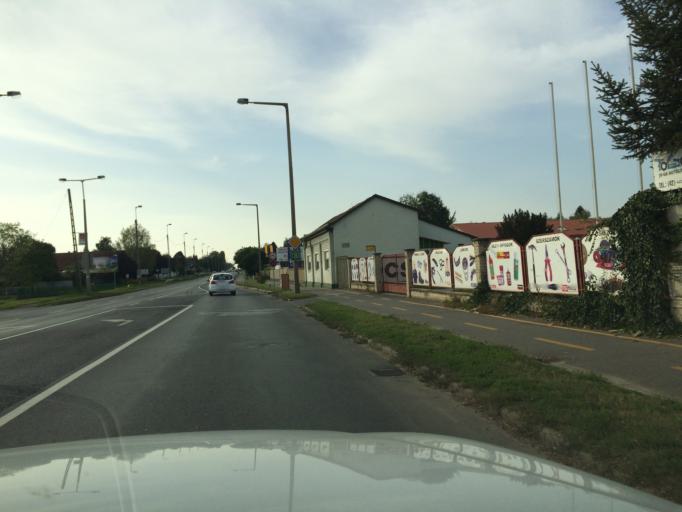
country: HU
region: Szabolcs-Szatmar-Bereg
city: Nyiregyhaza
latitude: 47.9573
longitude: 21.6933
